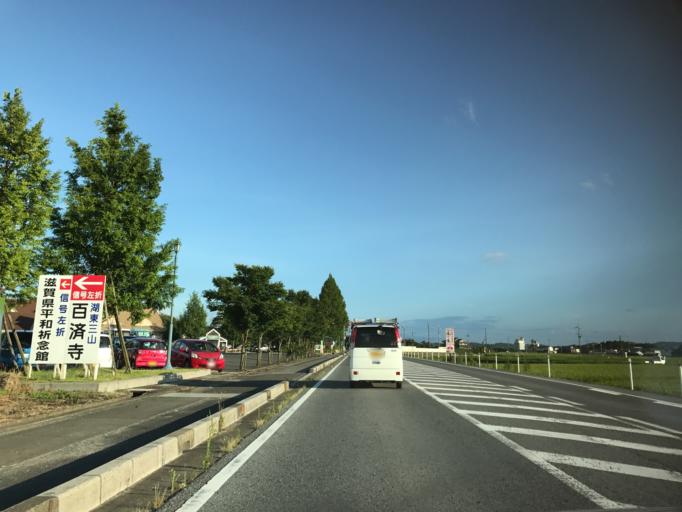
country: JP
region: Shiga Prefecture
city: Youkaichi
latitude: 35.1112
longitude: 136.2574
